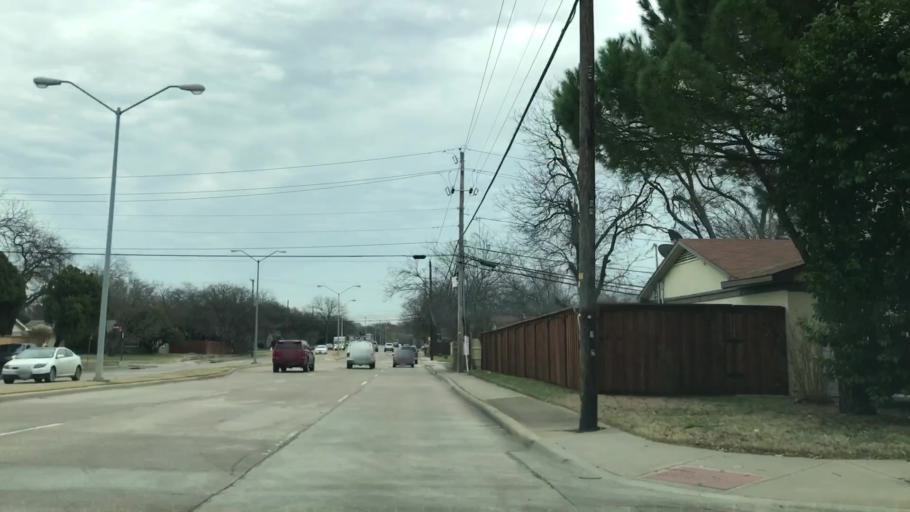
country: US
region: Texas
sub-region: Dallas County
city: Farmers Branch
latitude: 32.9319
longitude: -96.8859
